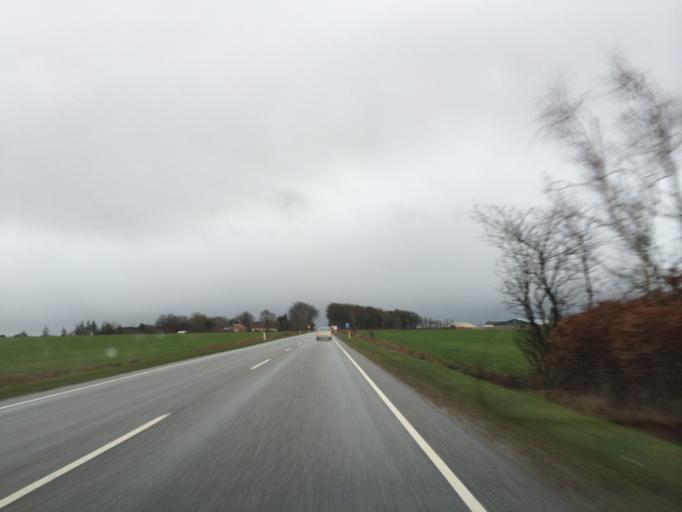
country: DK
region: South Denmark
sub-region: Varde Kommune
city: Varde
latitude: 55.7451
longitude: 8.4935
